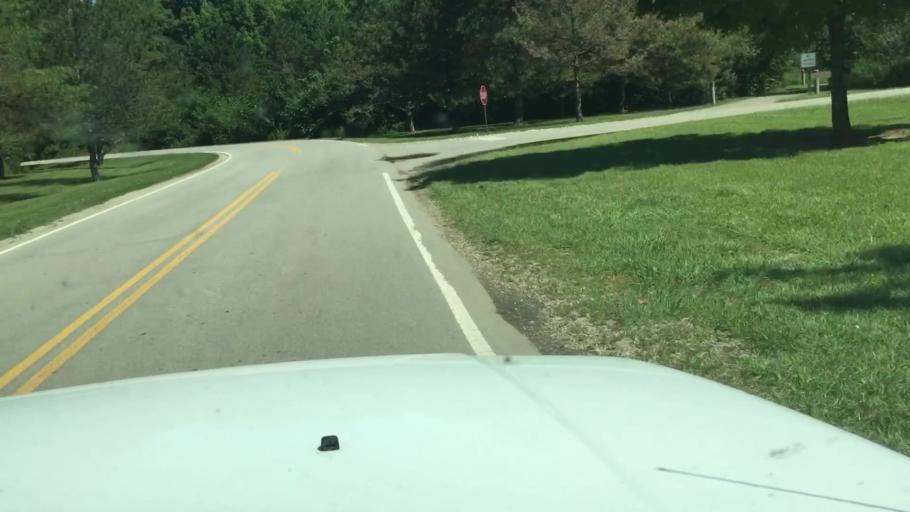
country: US
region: Ohio
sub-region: Madison County
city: Mount Sterling
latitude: 39.6391
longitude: -83.2417
